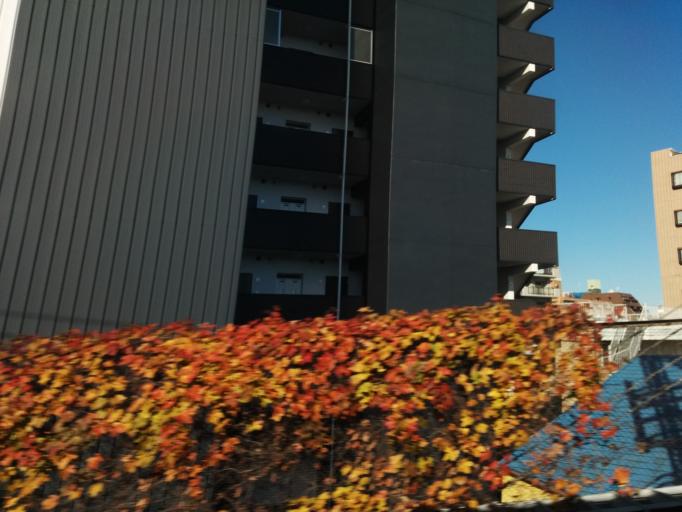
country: JP
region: Kanagawa
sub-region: Kawasaki-shi
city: Kawasaki
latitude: 35.5780
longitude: 139.6639
